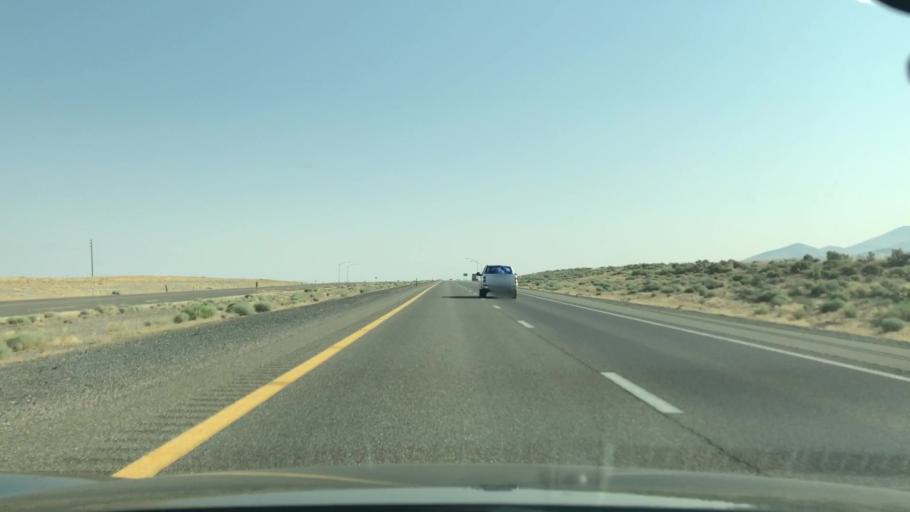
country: US
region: Nevada
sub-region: Humboldt County
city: Winnemucca
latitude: 40.7817
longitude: -118.0035
